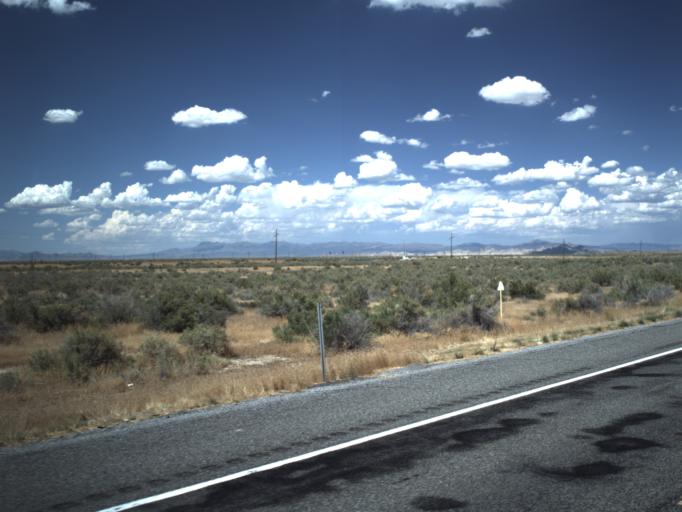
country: US
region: Utah
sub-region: Millard County
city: Delta
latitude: 39.4364
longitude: -112.4602
